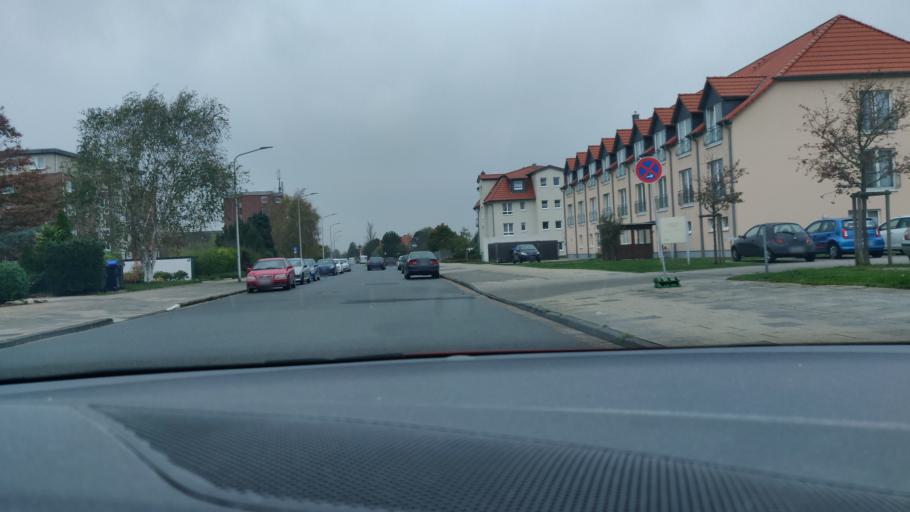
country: DE
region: Lower Saxony
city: Cuxhaven
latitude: 53.8695
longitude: 8.6870
